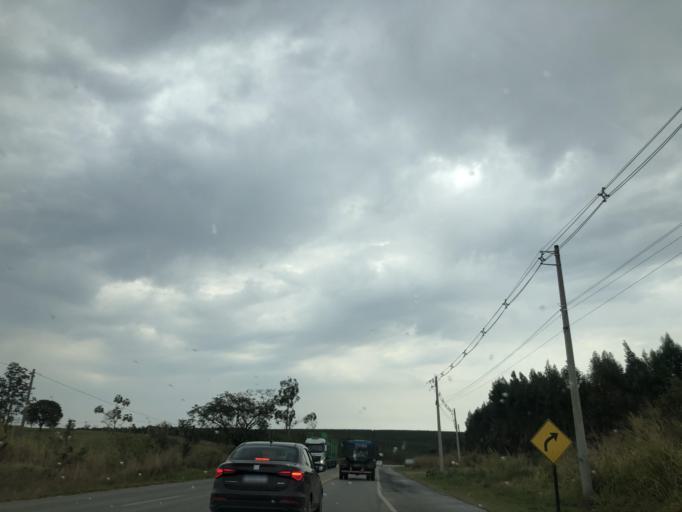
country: BR
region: Sao Paulo
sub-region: Salto De Pirapora
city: Salto de Pirapora
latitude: -23.6867
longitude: -47.6065
